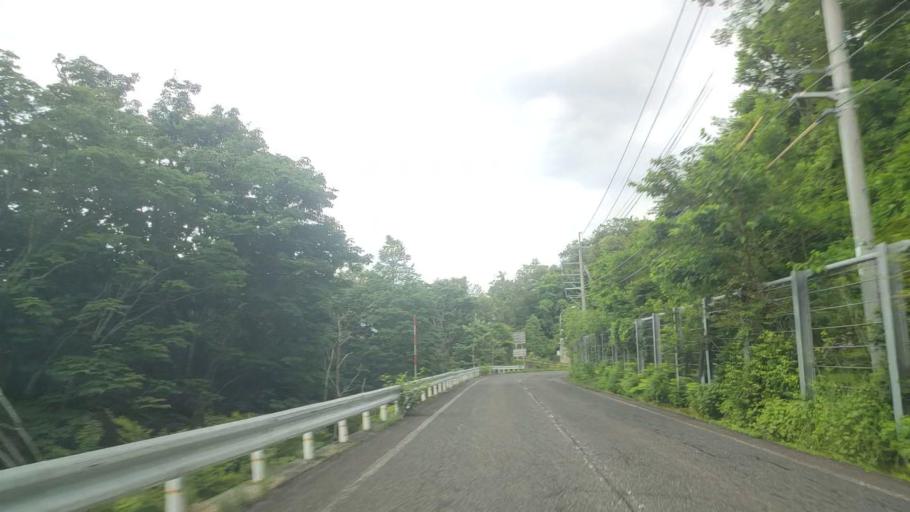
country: JP
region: Tottori
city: Kurayoshi
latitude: 35.3135
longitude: 134.0029
